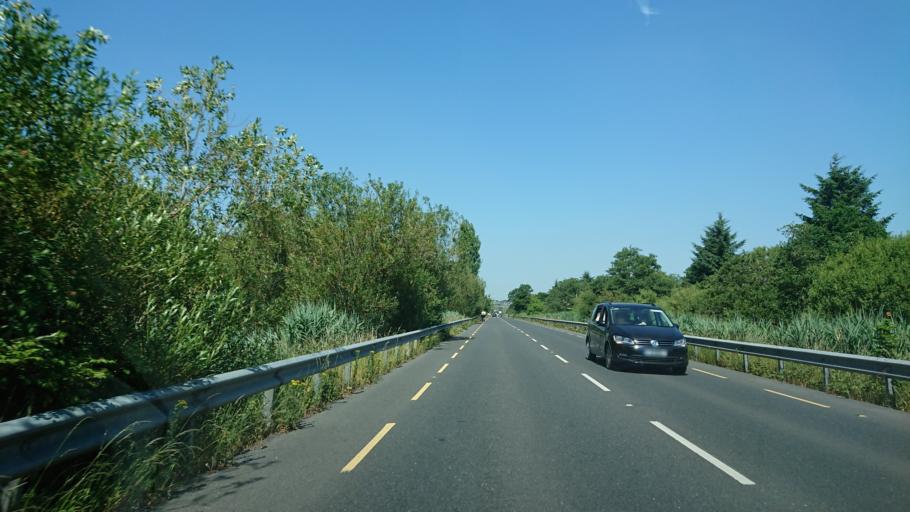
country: IE
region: Munster
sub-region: Waterford
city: Waterford
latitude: 52.2392
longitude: -7.1211
